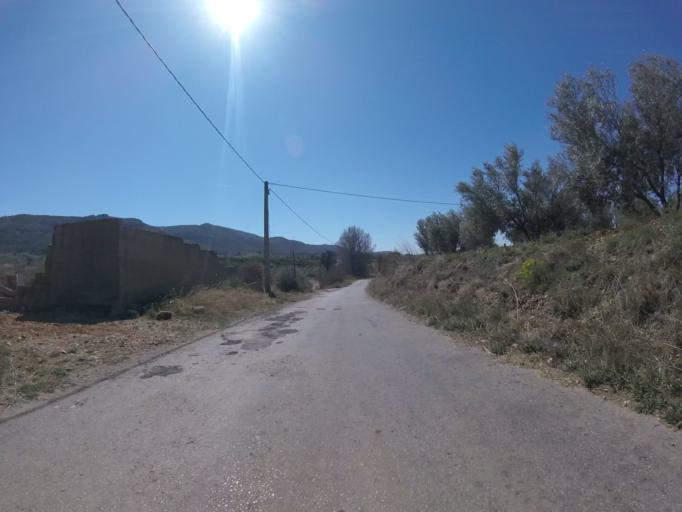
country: ES
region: Valencia
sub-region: Provincia de Castello
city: Chert/Xert
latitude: 40.4136
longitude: 0.1749
